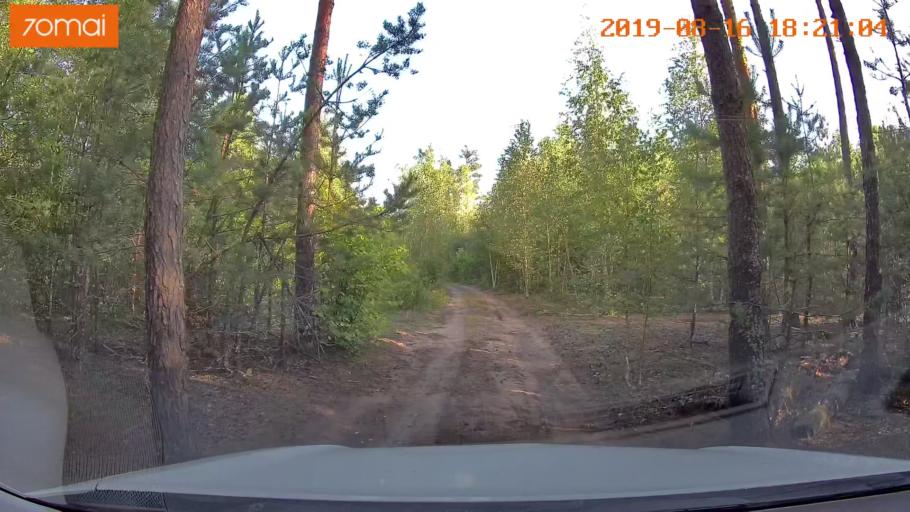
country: BY
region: Mogilev
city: Asipovichy
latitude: 53.2068
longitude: 28.6336
